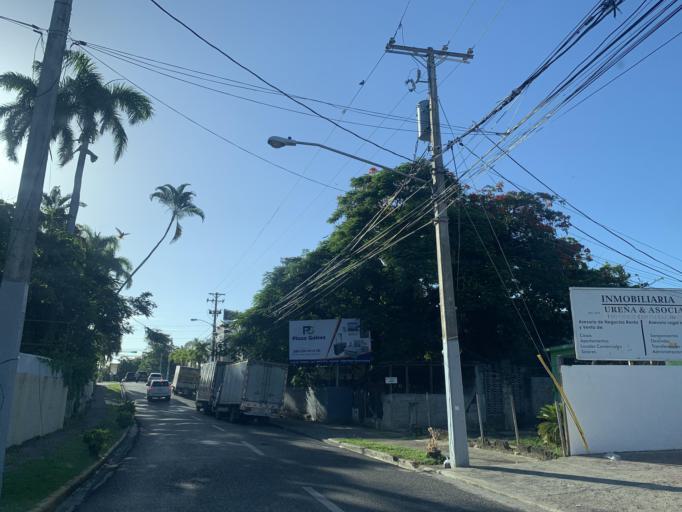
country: DO
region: Puerto Plata
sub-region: Puerto Plata
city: Puerto Plata
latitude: 19.7944
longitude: -70.6864
